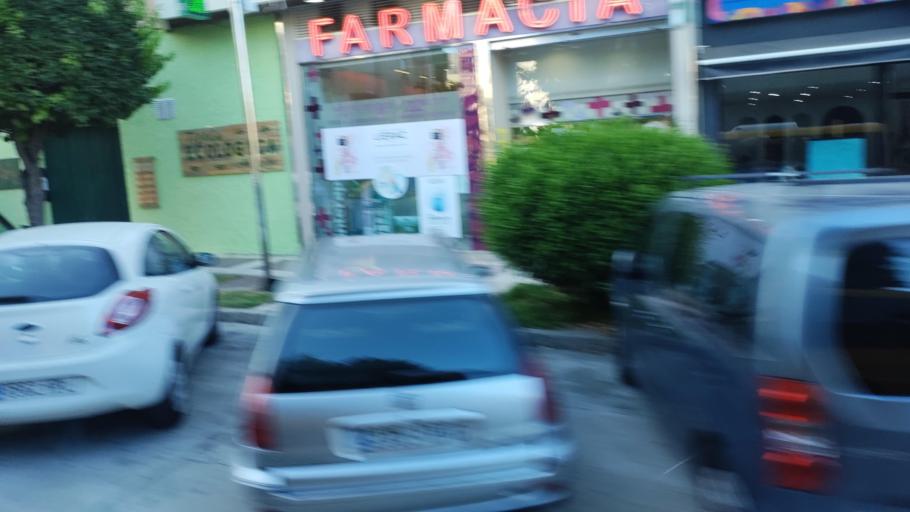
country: ES
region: Andalusia
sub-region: Provincia de Malaga
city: Torremolinos
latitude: 36.6292
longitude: -4.5000
